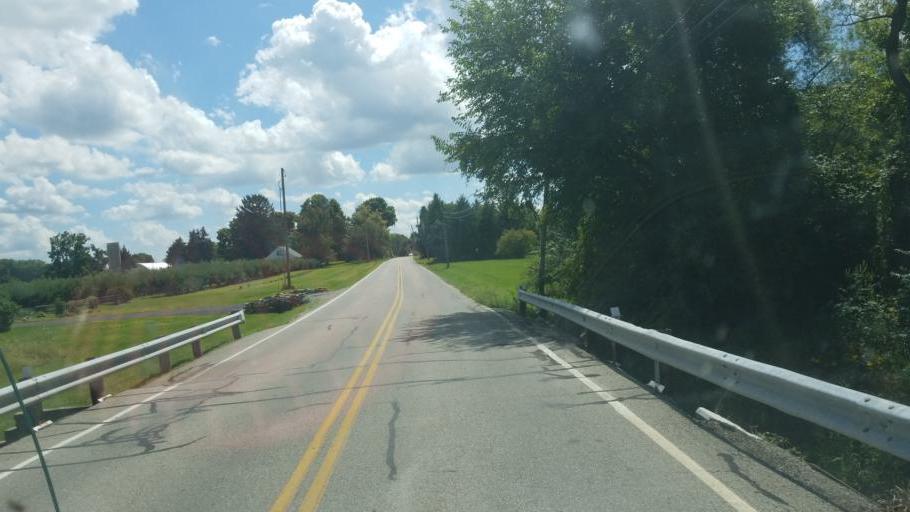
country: US
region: Ohio
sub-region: Marion County
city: Marion
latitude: 40.5396
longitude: -83.1369
